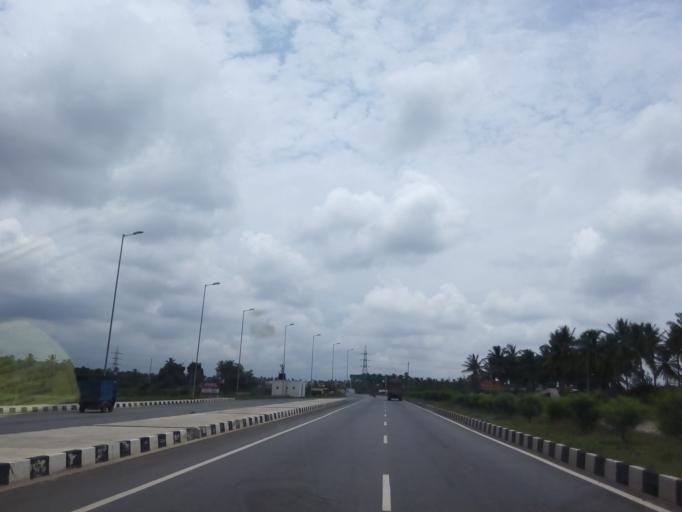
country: IN
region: Karnataka
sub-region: Hassan
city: Hassan
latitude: 12.9982
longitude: 76.1475
